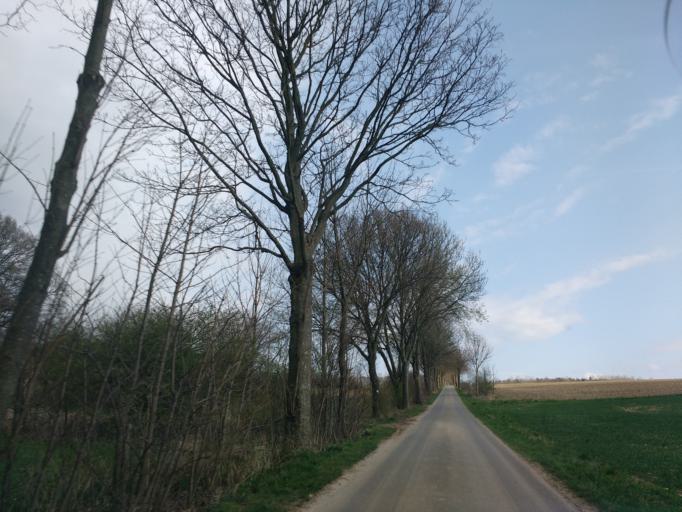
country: DE
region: North Rhine-Westphalia
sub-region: Regierungsbezirk Detmold
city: Schlangen
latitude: 51.7621
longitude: 8.8672
